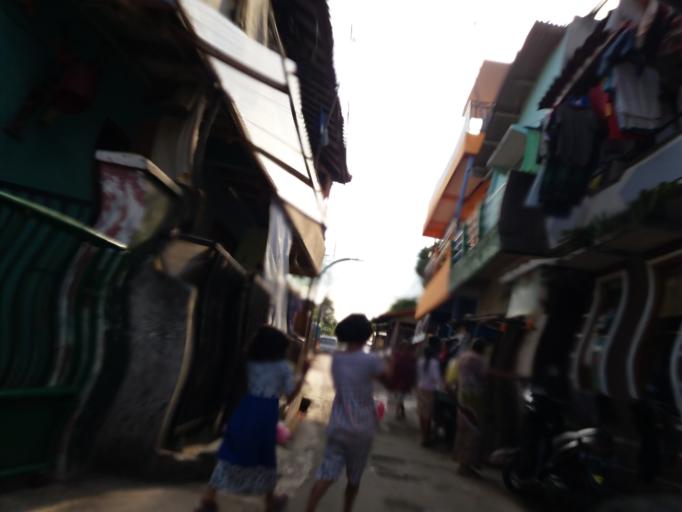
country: ID
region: West Java
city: Bandung
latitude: -6.9542
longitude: 107.6373
